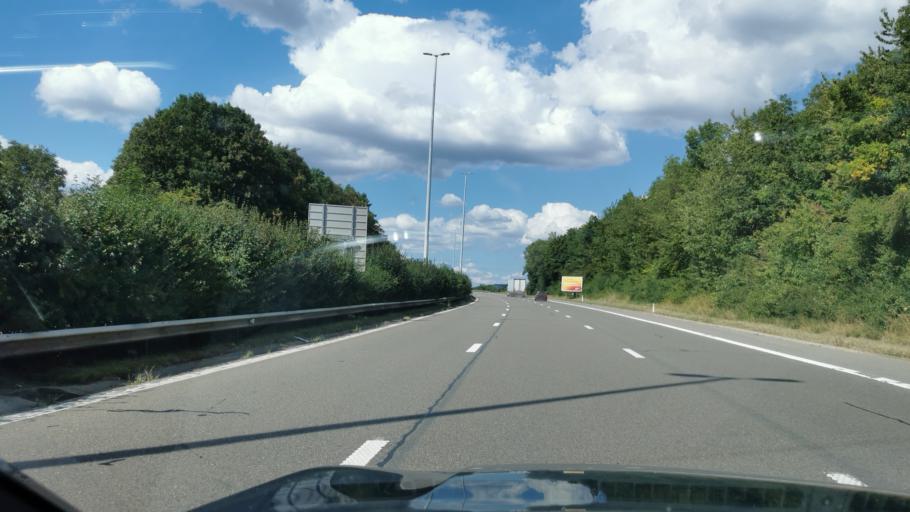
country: BE
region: Wallonia
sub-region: Province du Luxembourg
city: Aubange
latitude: 49.5685
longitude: 5.8214
